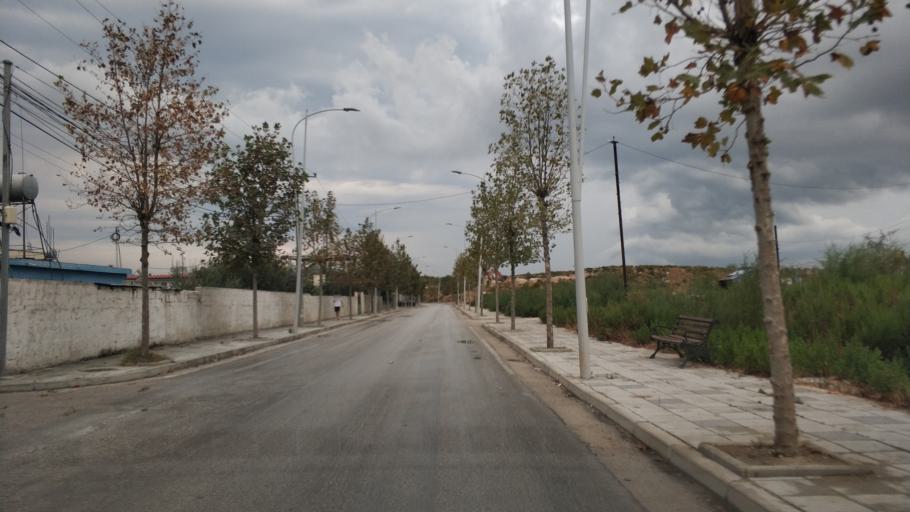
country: AL
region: Vlore
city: Vlore
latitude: 40.4854
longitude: 19.4698
